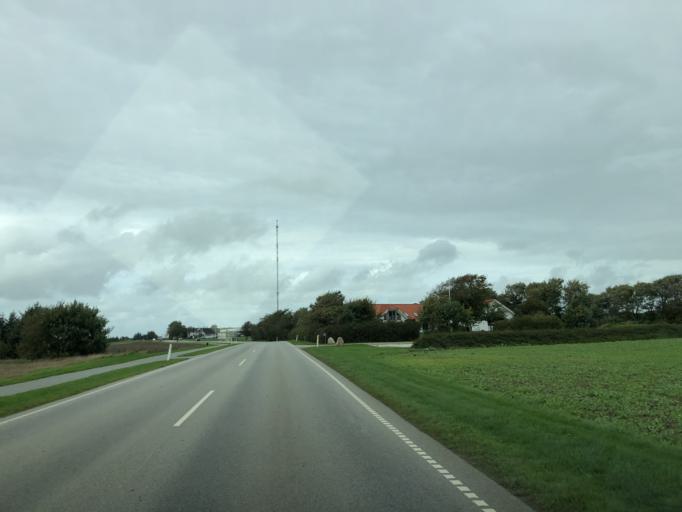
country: DK
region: North Denmark
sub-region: Thisted Kommune
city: Thisted
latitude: 56.9694
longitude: 8.6863
